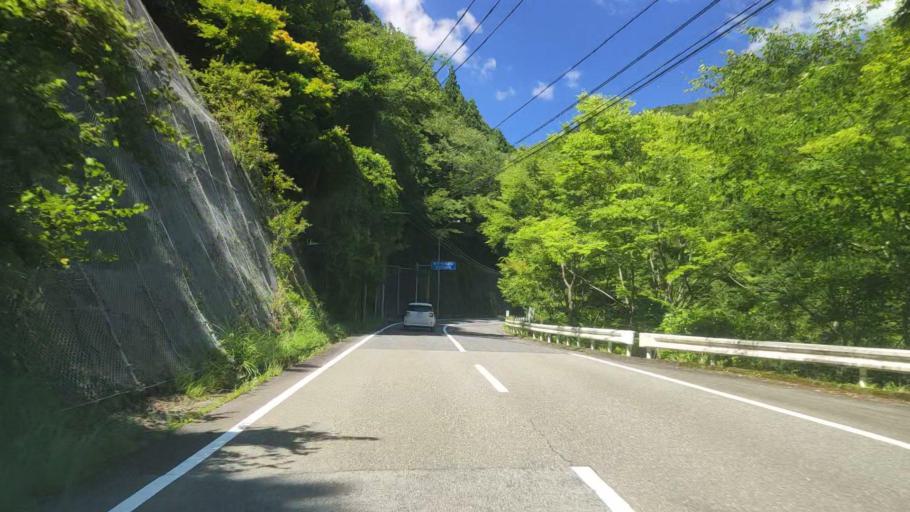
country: JP
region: Mie
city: Owase
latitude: 34.1959
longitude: 135.9990
